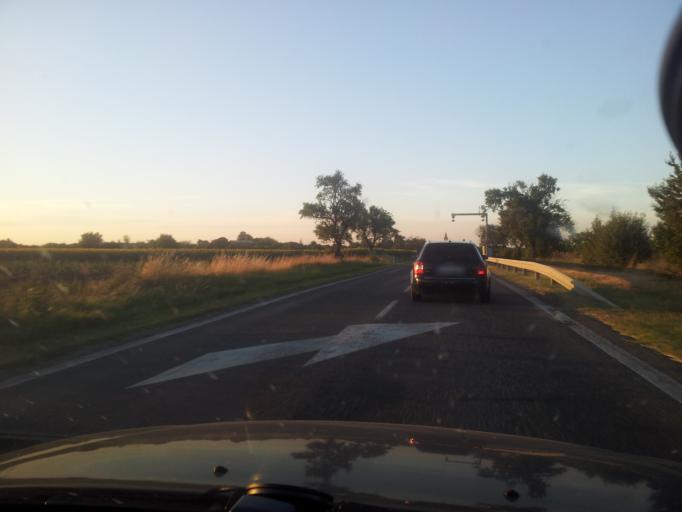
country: SK
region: Nitriansky
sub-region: Okres Nove Zamky
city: Sturovo
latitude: 47.8793
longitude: 18.6420
